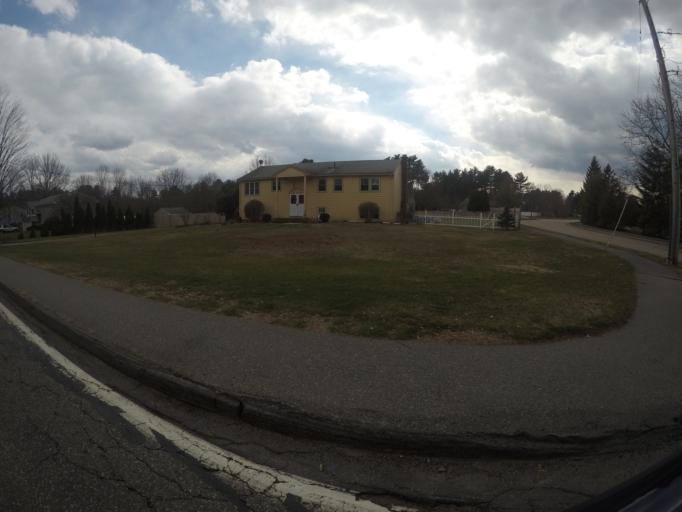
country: US
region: Massachusetts
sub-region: Bristol County
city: Easton
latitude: 42.0578
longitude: -71.1273
